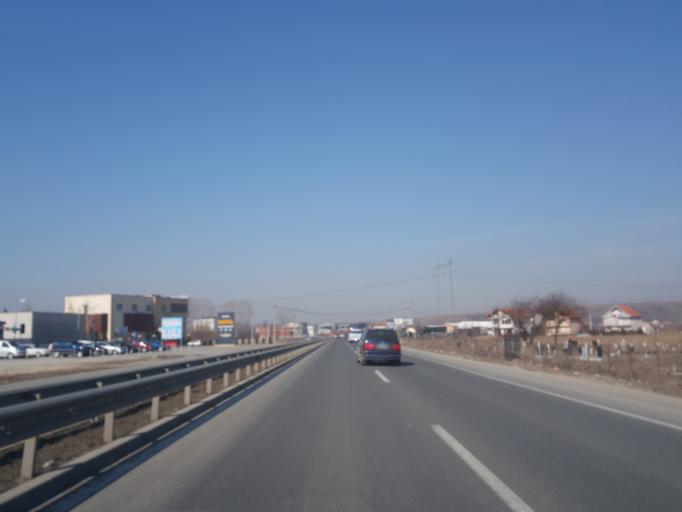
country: XK
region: Pristina
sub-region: Komuna e Obiliqit
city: Obiliq
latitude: 42.7306
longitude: 21.0744
